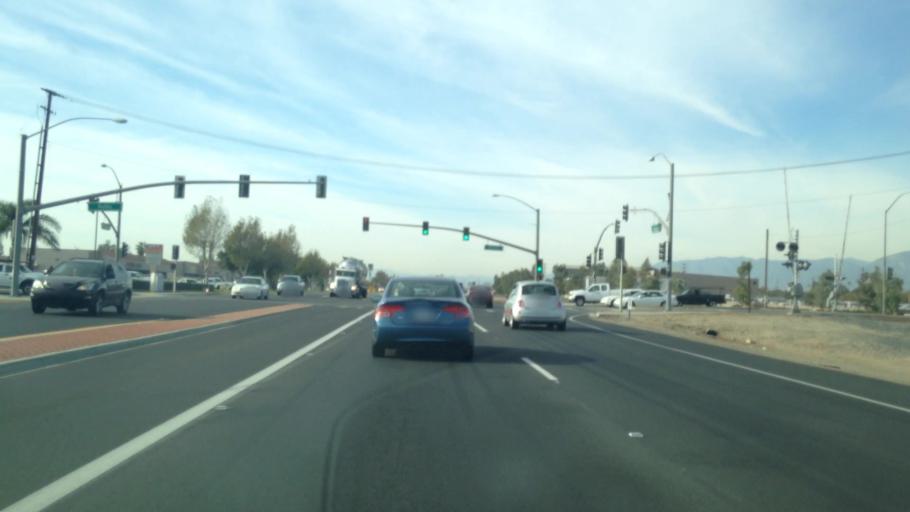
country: US
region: California
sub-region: Riverside County
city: Glen Avon
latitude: 34.0035
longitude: -117.4971
